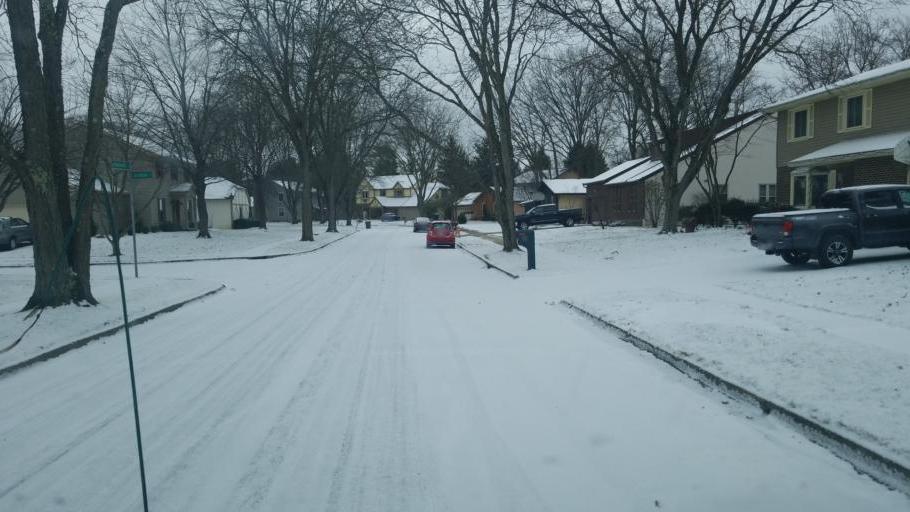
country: US
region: Ohio
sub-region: Delaware County
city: Powell
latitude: 40.1284
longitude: -83.0809
